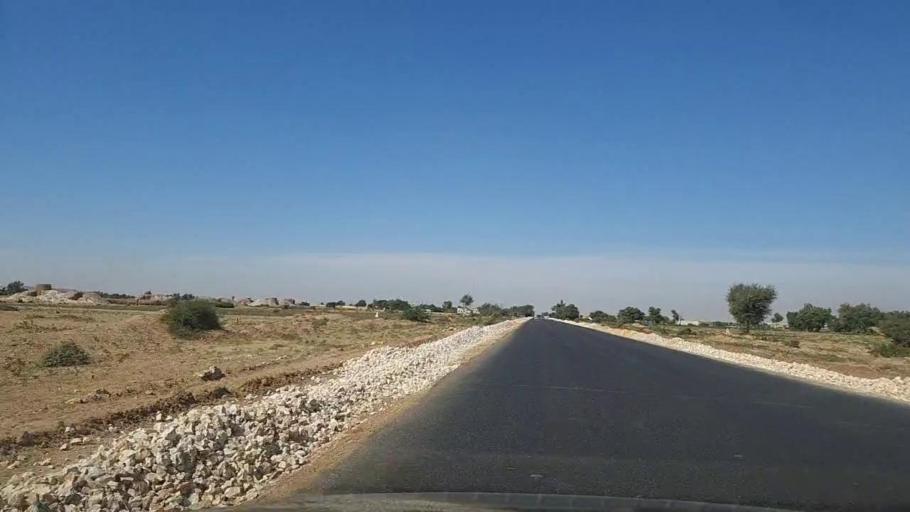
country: PK
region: Sindh
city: Kotri
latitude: 25.2811
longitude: 68.2118
